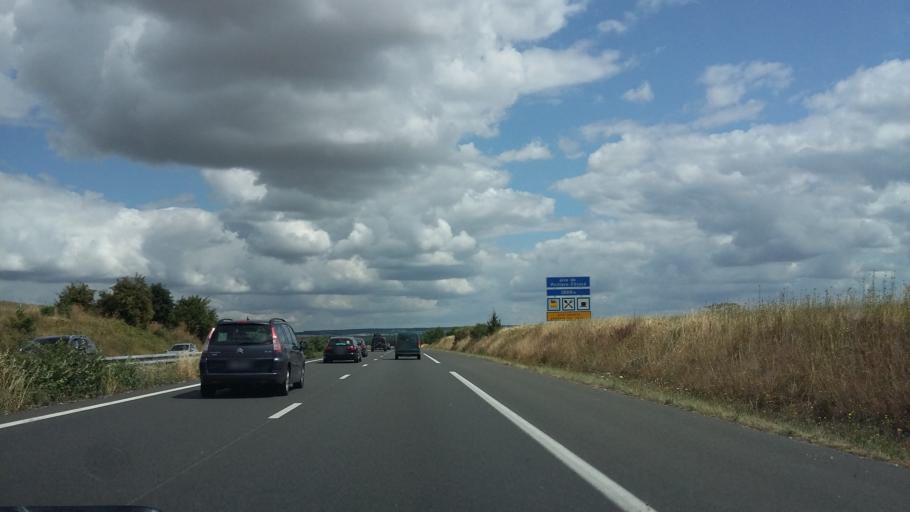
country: FR
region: Poitou-Charentes
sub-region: Departement de la Vienne
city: Jaunay-Clan
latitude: 46.6879
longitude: 0.3642
